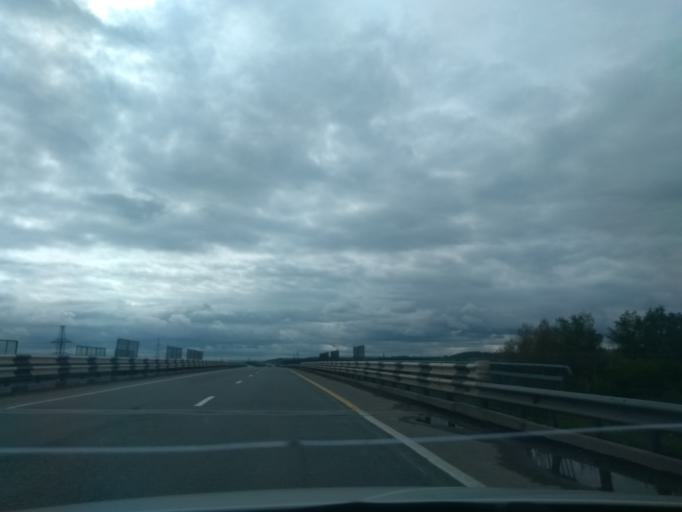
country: RU
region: Perm
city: Froly
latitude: 57.9312
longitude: 56.2968
